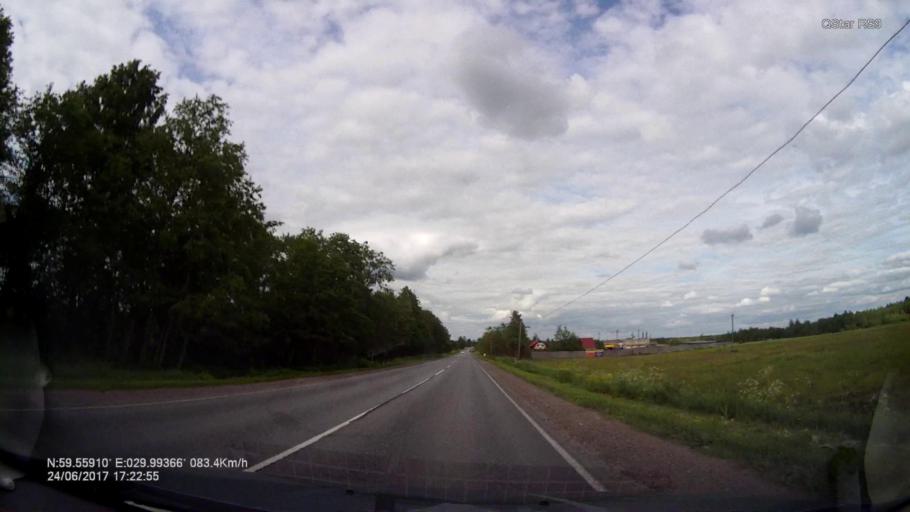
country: RU
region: Leningrad
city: Voyskovitsy
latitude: 59.5594
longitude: 29.9945
